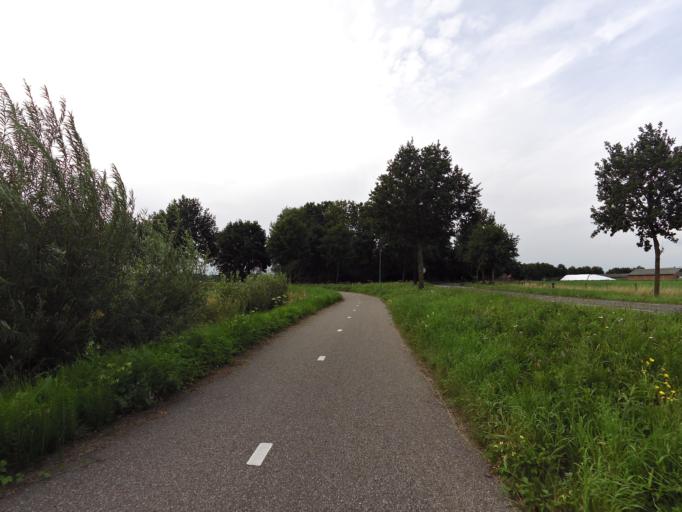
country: NL
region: Gelderland
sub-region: Gemeente Doesburg
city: Doesburg
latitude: 51.9825
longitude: 6.1284
